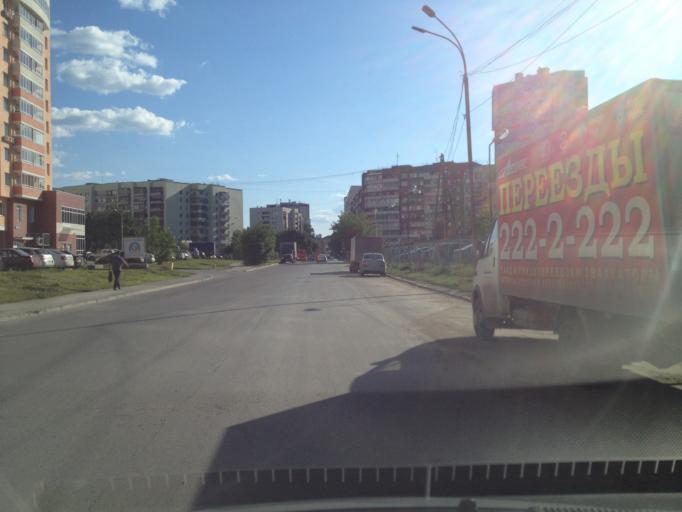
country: RU
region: Sverdlovsk
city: Yekaterinburg
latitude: 56.9089
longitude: 60.6224
